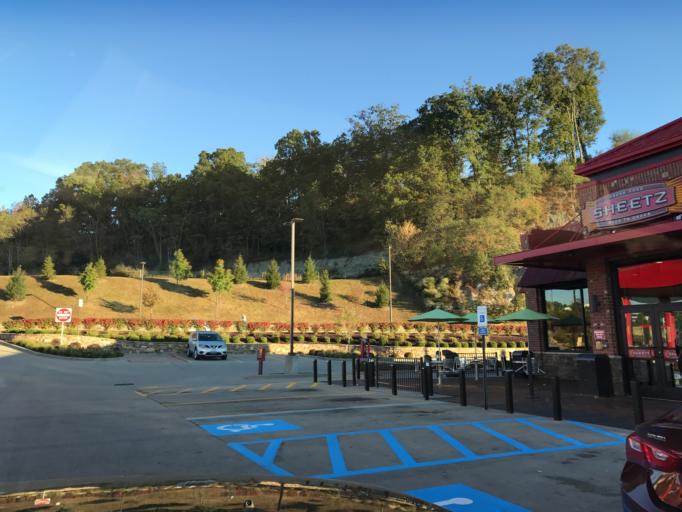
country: US
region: West Virginia
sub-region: Harrison County
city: Bridgeport
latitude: 39.3333
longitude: -80.2393
